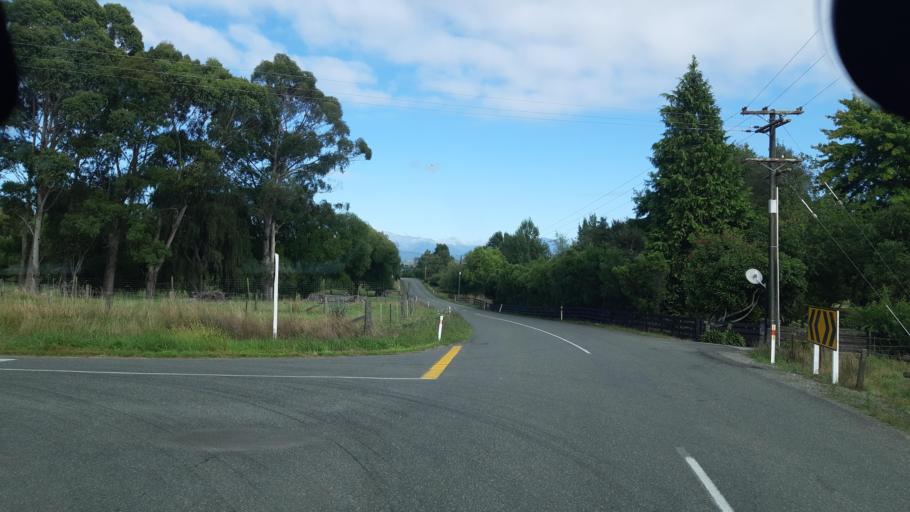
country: NZ
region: Tasman
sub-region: Tasman District
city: Mapua
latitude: -41.2417
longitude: 173.0393
